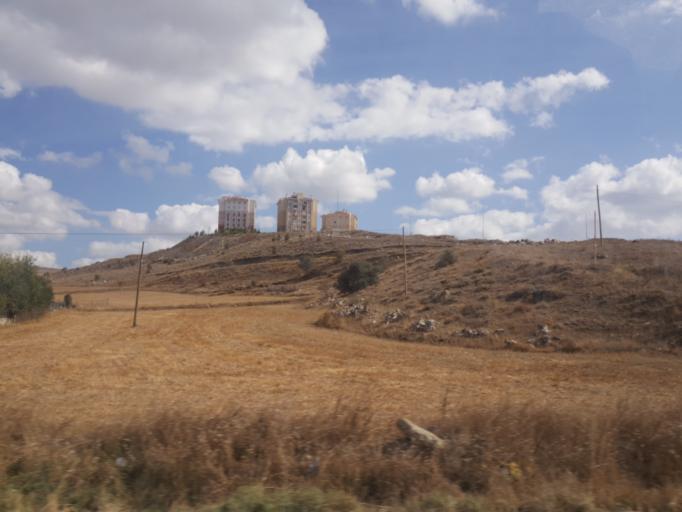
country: TR
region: Tokat
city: Artova
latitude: 40.1164
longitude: 36.3115
